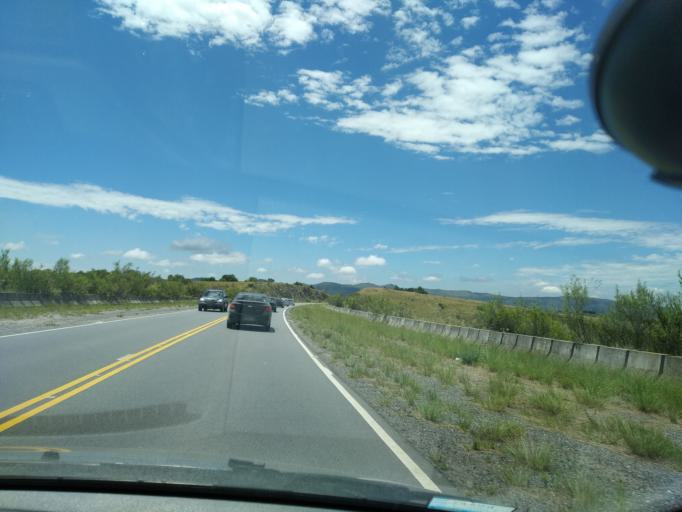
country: AR
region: Cordoba
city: Cuesta Blanca
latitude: -31.5838
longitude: -64.6257
